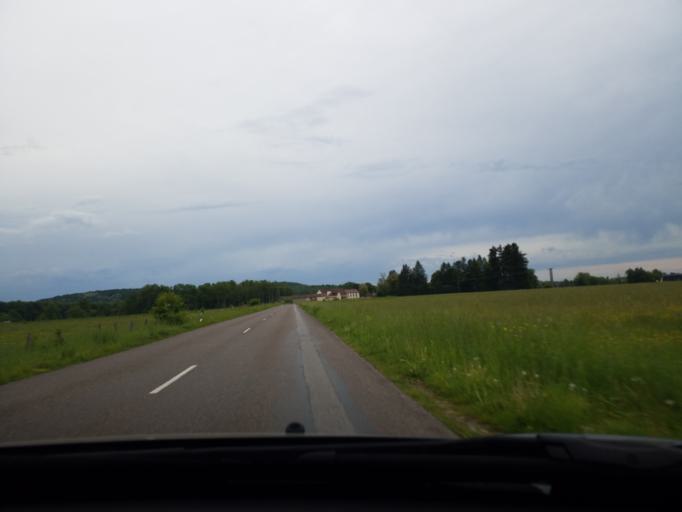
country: FR
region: Franche-Comte
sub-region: Departement de la Haute-Saone
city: Corbenay
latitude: 47.8862
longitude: 6.3149
